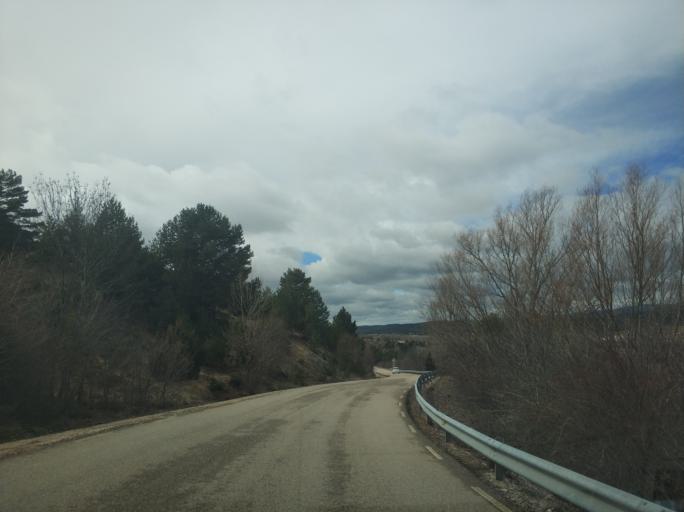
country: ES
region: Castille and Leon
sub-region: Provincia de Soria
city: Abejar
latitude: 41.7973
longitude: -2.7733
